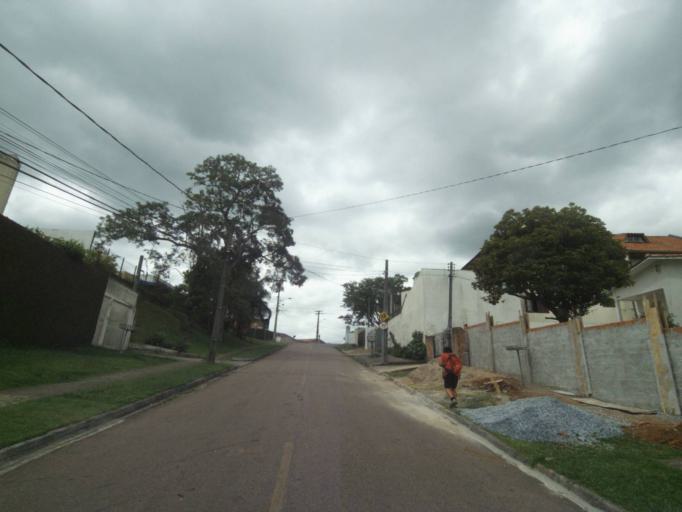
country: BR
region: Parana
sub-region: Curitiba
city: Curitiba
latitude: -25.3880
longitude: -49.2862
